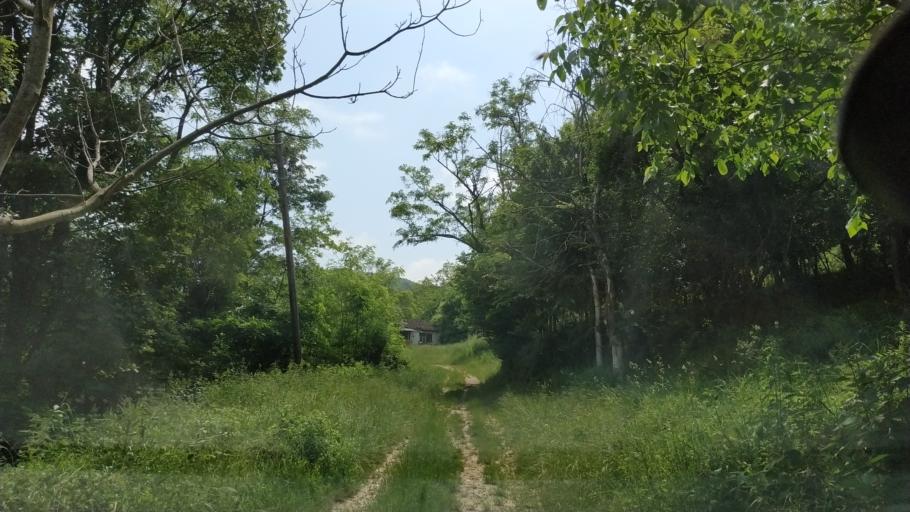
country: RS
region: Central Serbia
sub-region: Nisavski Okrug
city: Merosina
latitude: 43.4101
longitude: 21.7147
